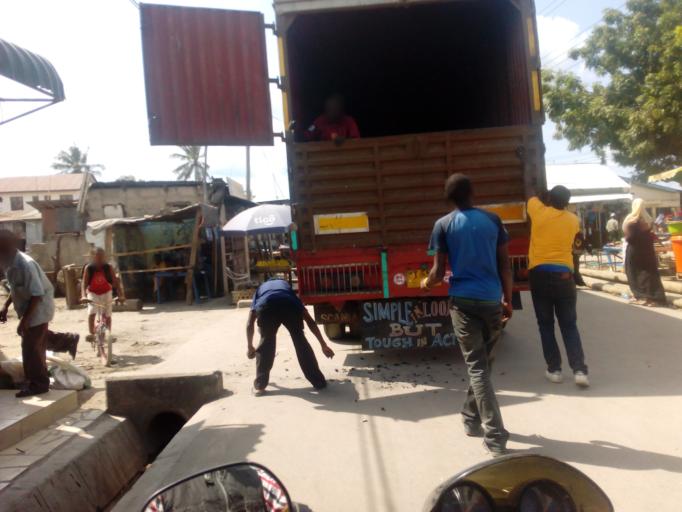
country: TZ
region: Dar es Salaam
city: Dar es Salaam
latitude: -6.8395
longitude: 39.2737
